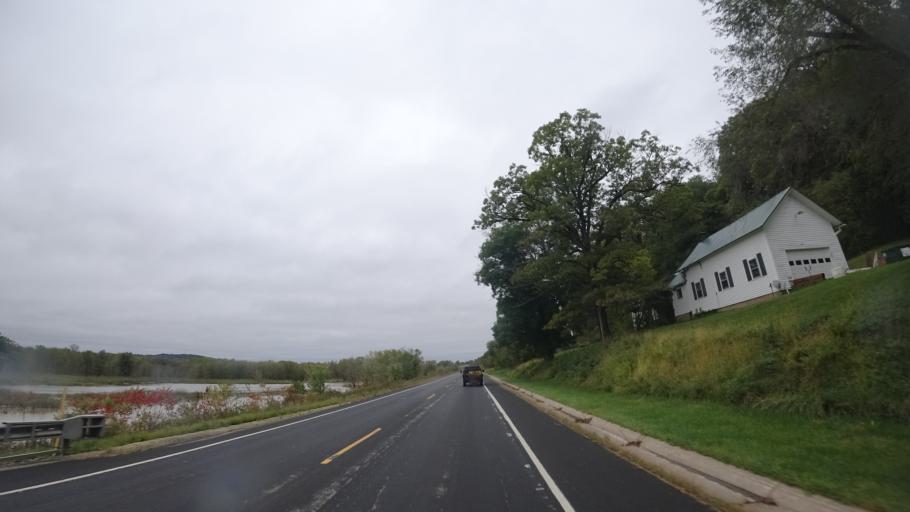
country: US
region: Wisconsin
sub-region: Grant County
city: Boscobel
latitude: 43.1192
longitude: -90.7842
